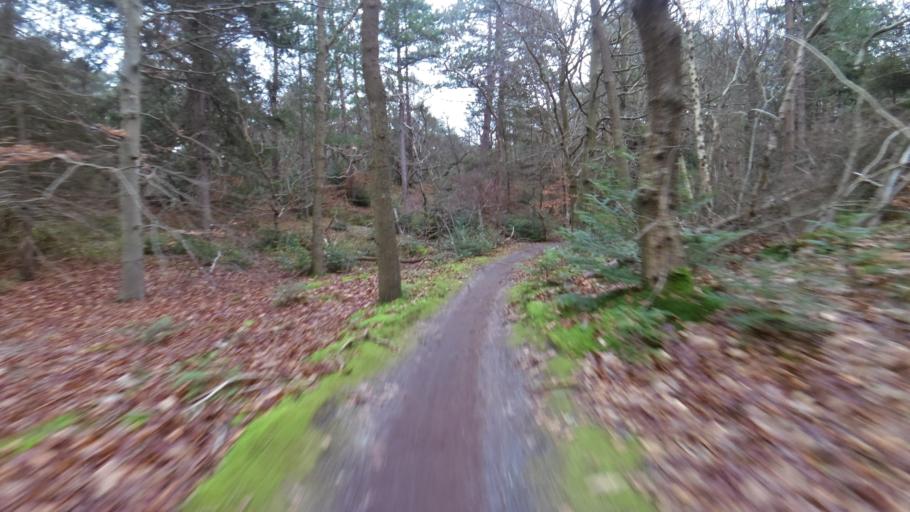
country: NL
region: North Holland
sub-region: Gemeente Alkmaar
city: Alkmaar
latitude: 52.6829
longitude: 4.6890
